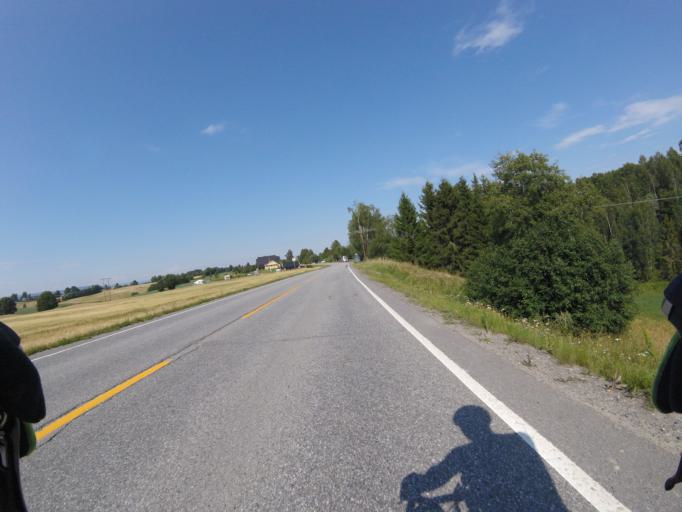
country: NO
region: Akershus
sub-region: Sorum
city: Frogner
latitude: 60.0482
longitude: 11.1189
